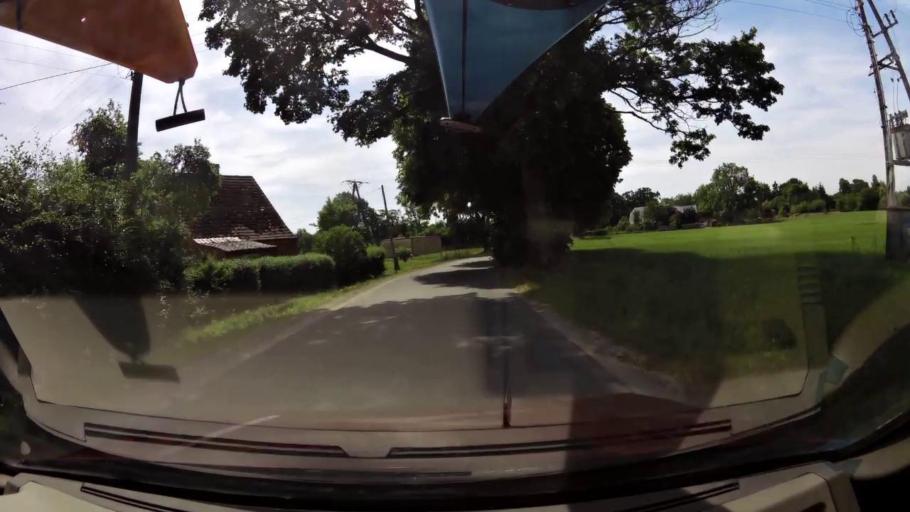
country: PL
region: West Pomeranian Voivodeship
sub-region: Powiat slawienski
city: Darlowo
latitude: 54.3096
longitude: 16.4805
